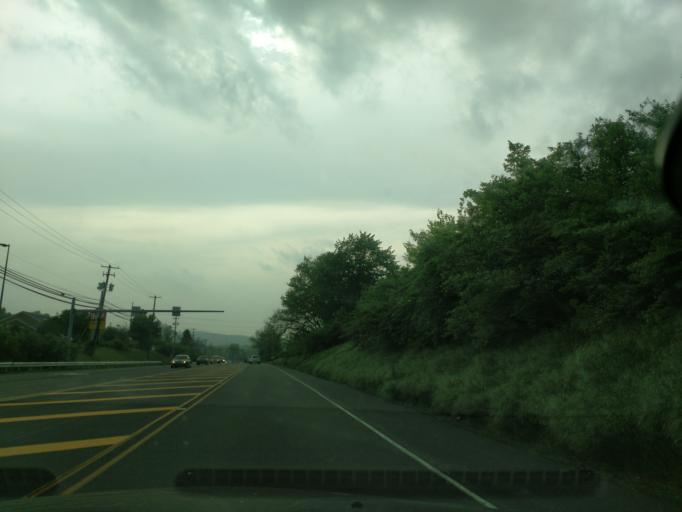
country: US
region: Pennsylvania
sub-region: Berks County
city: Wernersville
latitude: 40.3269
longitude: -76.0497
